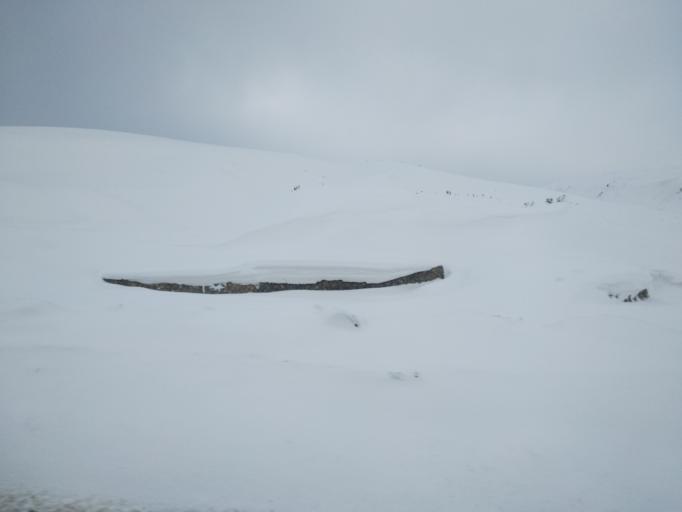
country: TR
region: Erzincan
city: Catalarmut
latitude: 39.8895
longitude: 39.3566
